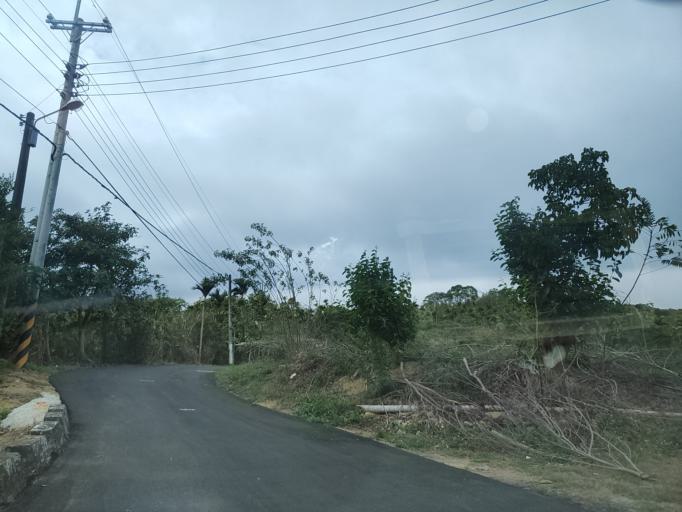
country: TW
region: Taiwan
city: Fengyuan
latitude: 24.3581
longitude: 120.7787
